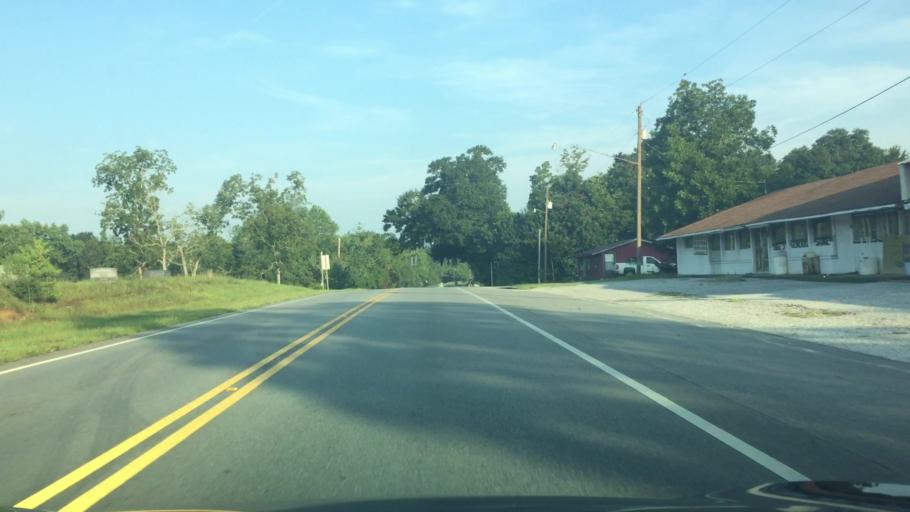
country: US
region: Alabama
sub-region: Covington County
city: Florala
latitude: 31.0113
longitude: -86.3523
